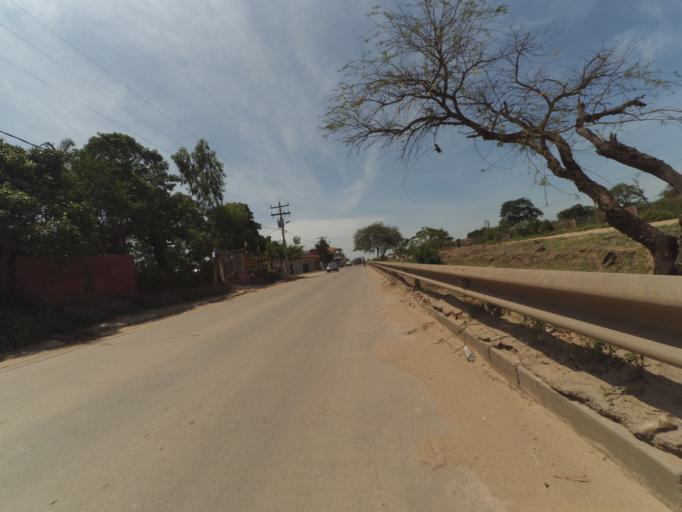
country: BO
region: Santa Cruz
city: Santa Cruz de la Sierra
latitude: -17.8344
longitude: -63.2401
